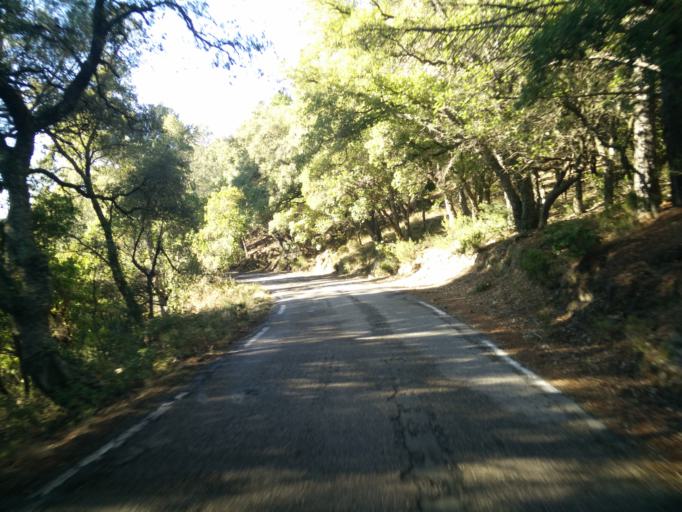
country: FR
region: Provence-Alpes-Cote d'Azur
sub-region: Departement du Var
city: La Garde-Freinet
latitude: 43.2542
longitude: 6.4072
